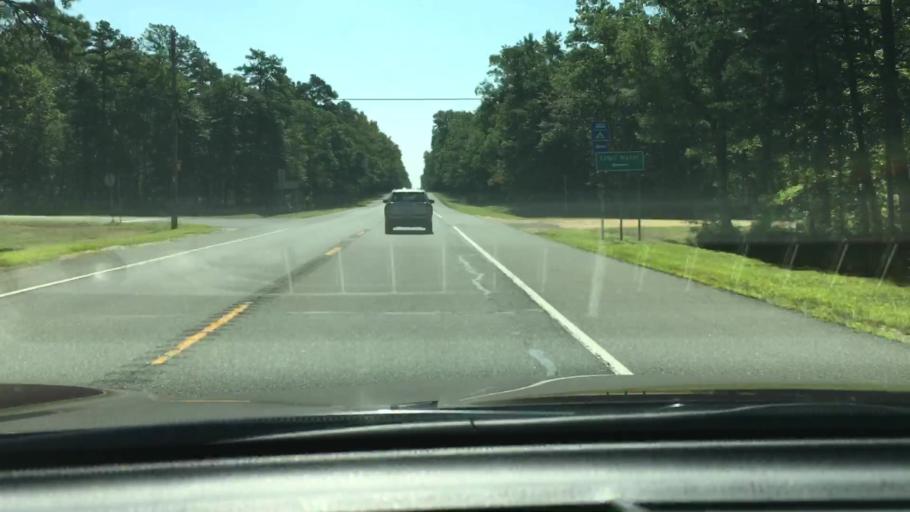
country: US
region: New Jersey
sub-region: Cumberland County
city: Laurel Lake
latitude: 39.3497
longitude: -74.9077
